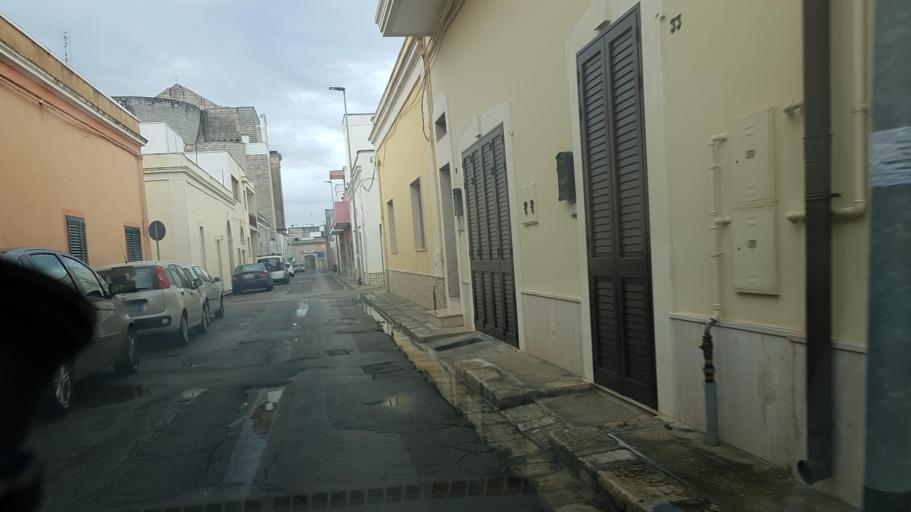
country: IT
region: Apulia
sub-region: Provincia di Lecce
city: Carmiano
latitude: 40.3439
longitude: 18.0469
